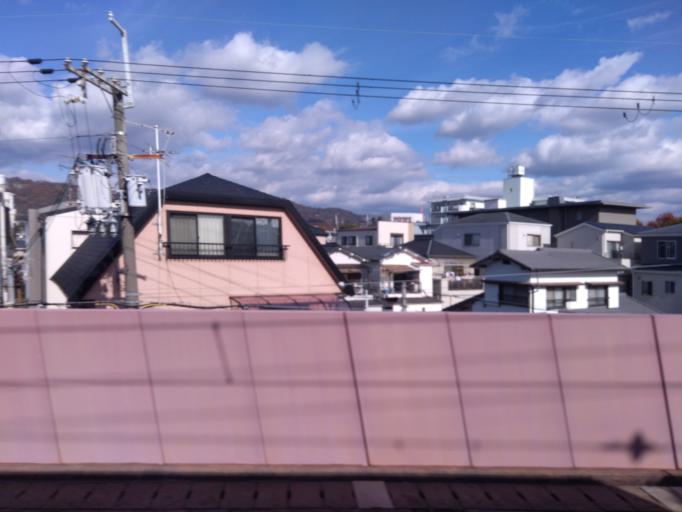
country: JP
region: Osaka
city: Ikeda
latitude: 34.8134
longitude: 135.4378
